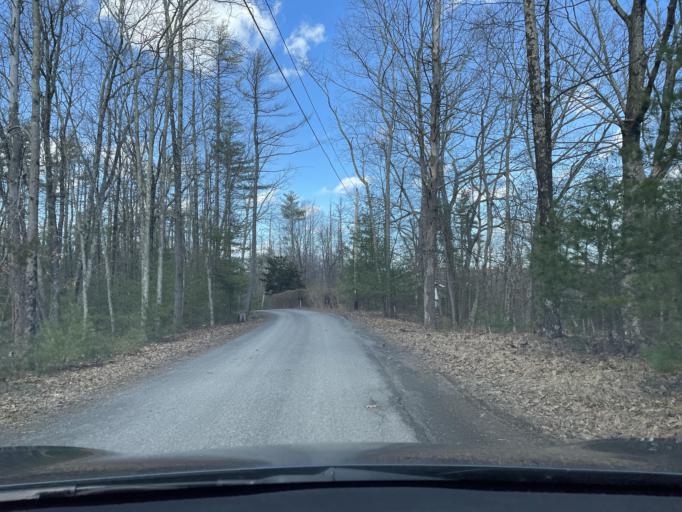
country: US
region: New York
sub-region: Ulster County
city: West Hurley
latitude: 41.9525
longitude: -74.1099
